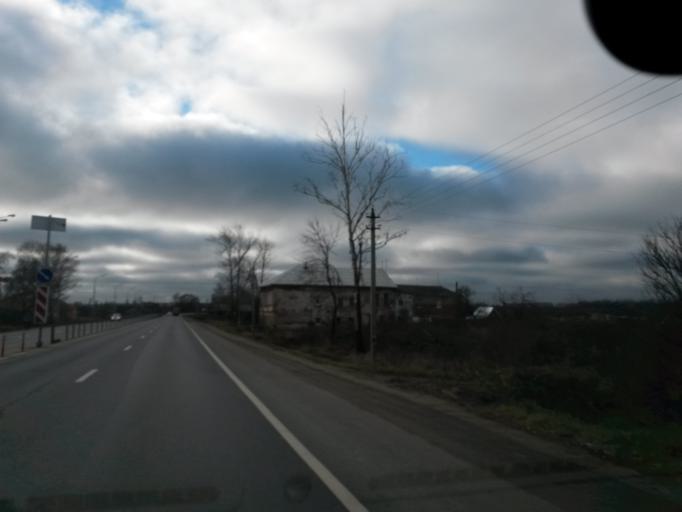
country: RU
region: Jaroslavl
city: Semibratovo
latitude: 57.3181
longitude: 39.5599
